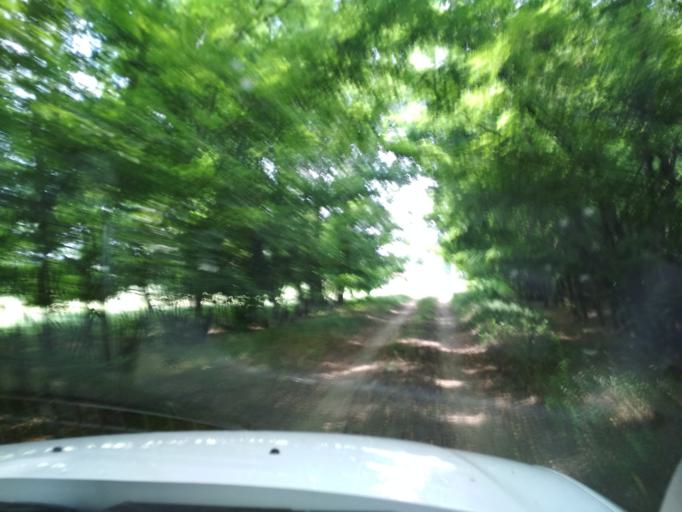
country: HU
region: Pest
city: Nagykata
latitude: 47.3965
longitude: 19.7667
